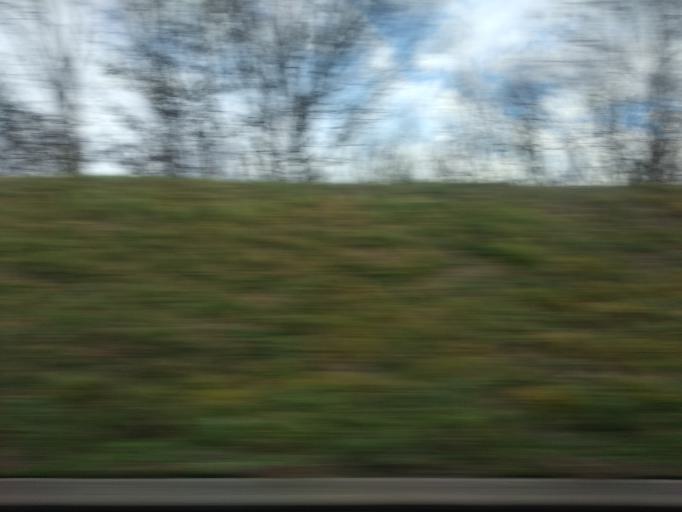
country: CH
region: Thurgau
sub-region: Muenchwilen District
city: Wangi
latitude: 47.5002
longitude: 8.9418
